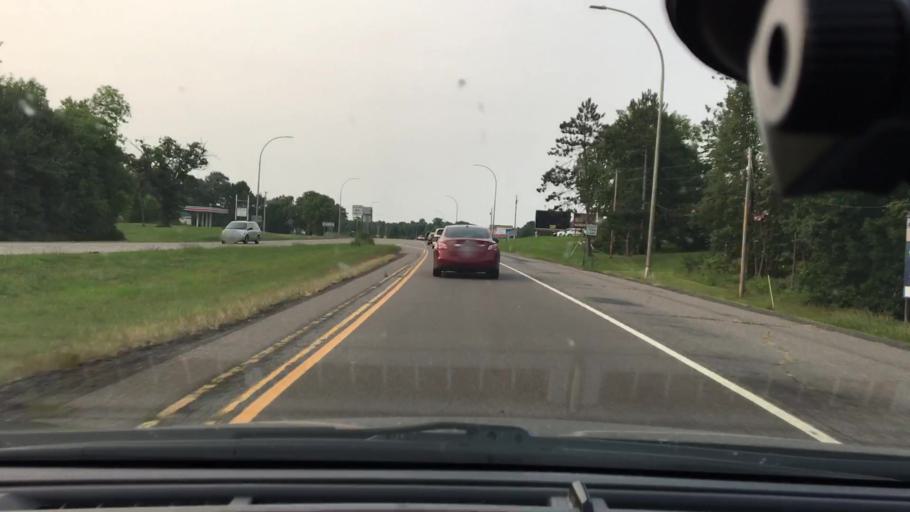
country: US
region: Minnesota
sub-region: Mille Lacs County
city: Vineland
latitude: 46.1046
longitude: -93.6445
